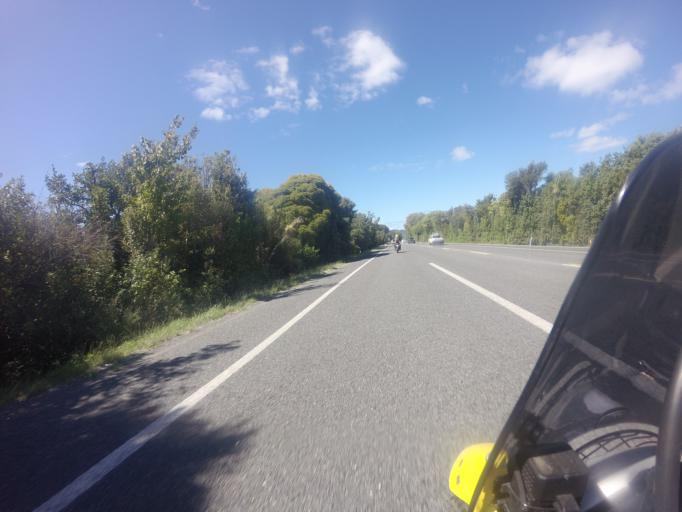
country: NZ
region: Bay of Plenty
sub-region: Whakatane District
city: Whakatane
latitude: -37.9513
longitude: 176.9550
